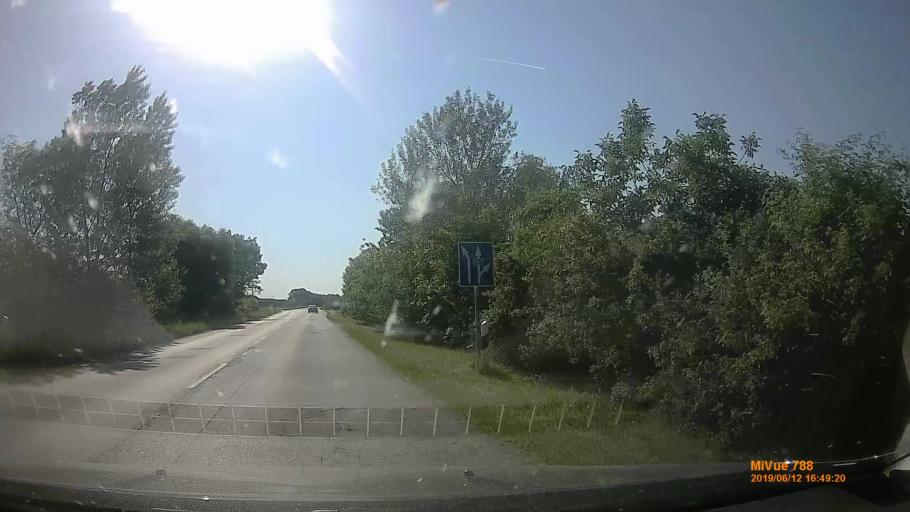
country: HU
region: Csongrad
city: Kiszombor
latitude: 46.1933
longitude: 20.4127
